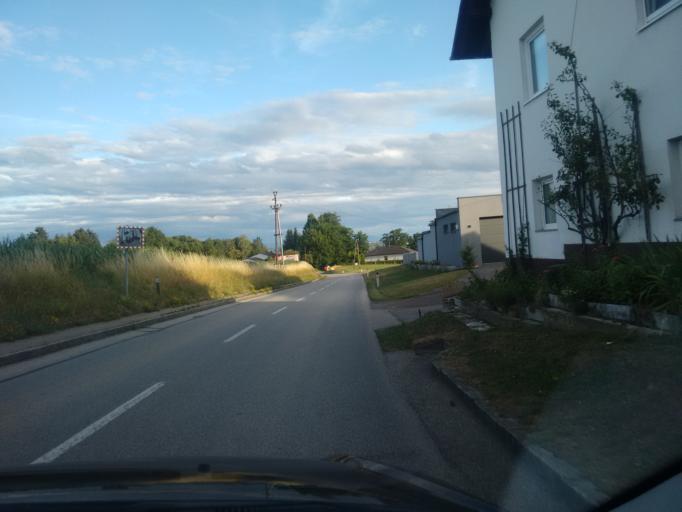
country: AT
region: Upper Austria
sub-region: Politischer Bezirk Urfahr-Umgebung
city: Walding
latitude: 48.3561
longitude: 14.1600
